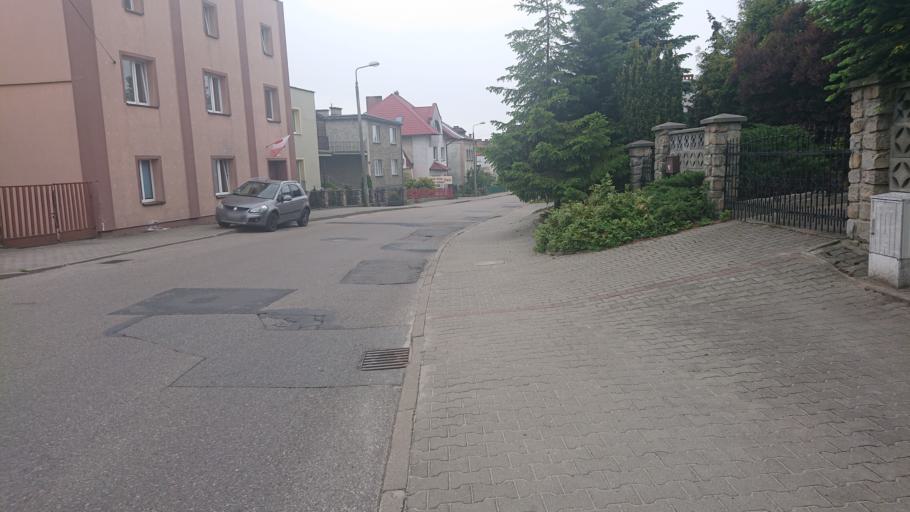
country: PL
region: Pomeranian Voivodeship
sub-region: Powiat chojnicki
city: Chojnice
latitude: 53.6975
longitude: 17.5660
